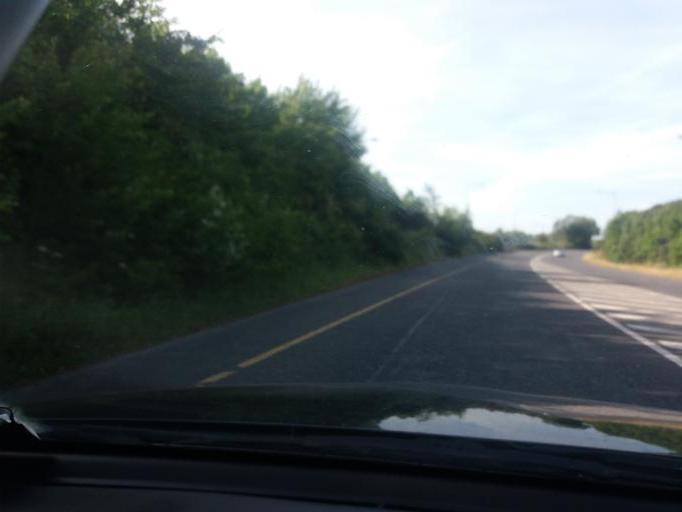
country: IE
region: Leinster
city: Balrothery
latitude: 53.5538
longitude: -6.2111
